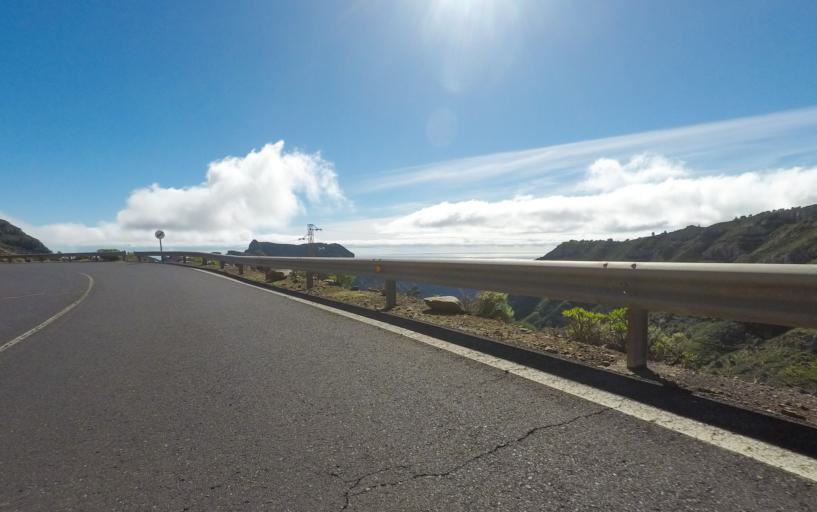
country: ES
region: Canary Islands
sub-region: Provincia de Santa Cruz de Tenerife
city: Alajero
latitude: 28.0933
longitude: -17.1969
